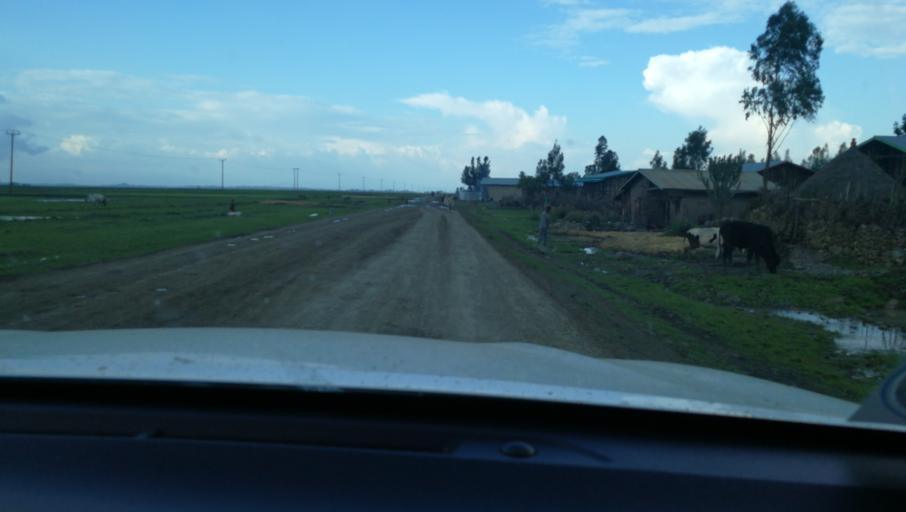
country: ET
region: Amhara
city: Were Ilu
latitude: 10.4406
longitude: 39.2556
